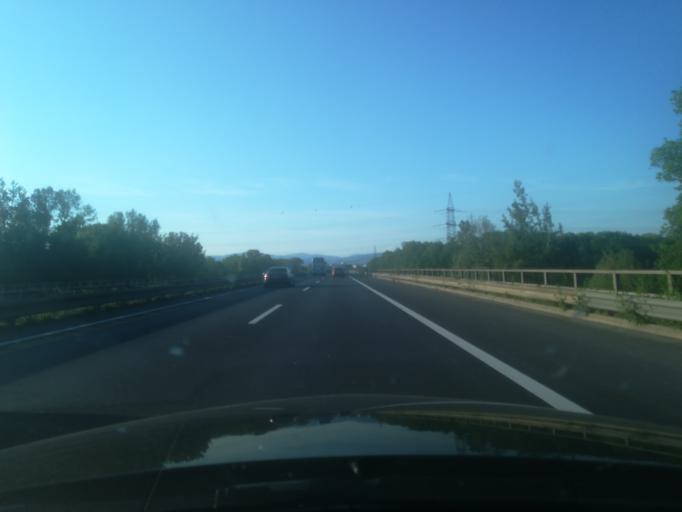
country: AT
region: Upper Austria
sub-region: Politischer Bezirk Linz-Land
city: Ansfelden
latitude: 48.2347
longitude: 14.2979
